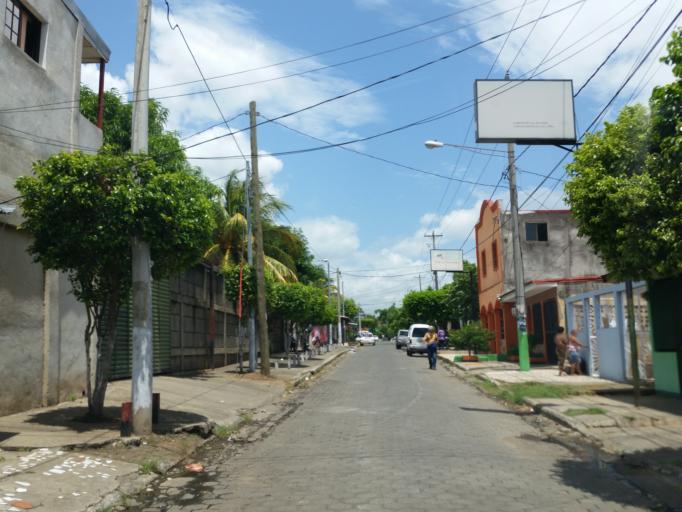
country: NI
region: Managua
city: Managua
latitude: 12.1196
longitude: -86.2485
